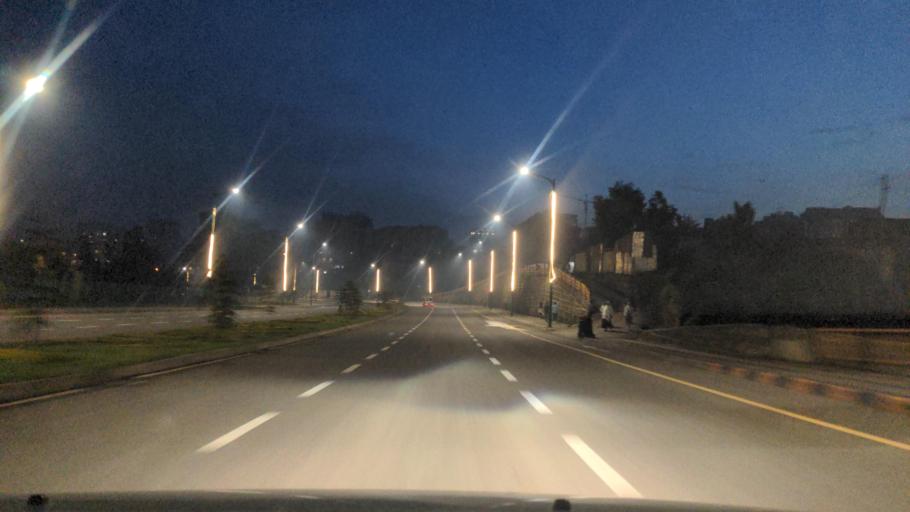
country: ET
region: Adis Abeba
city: Addis Ababa
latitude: 9.0063
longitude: 38.7749
